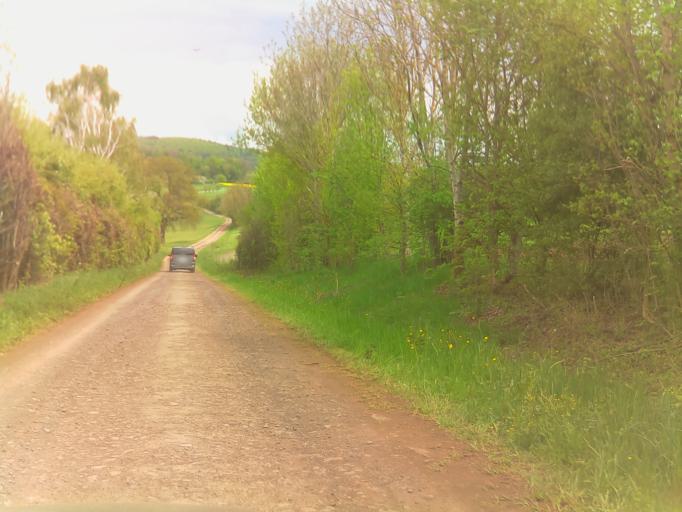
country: DE
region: Hesse
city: Gedern
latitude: 50.4320
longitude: 9.1879
